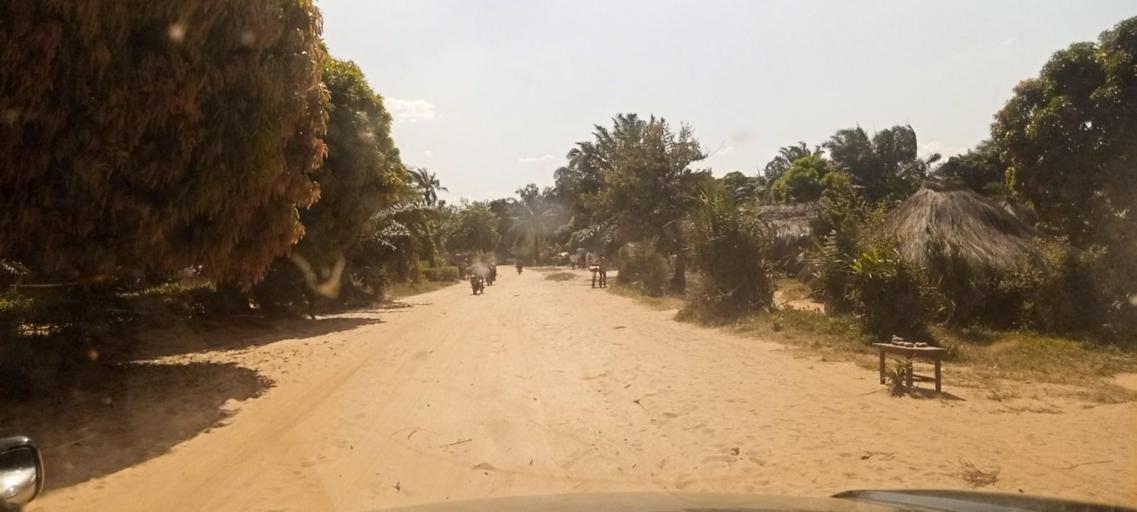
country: CD
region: Kasai-Oriental
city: Kabinda
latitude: -6.1314
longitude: 24.5078
